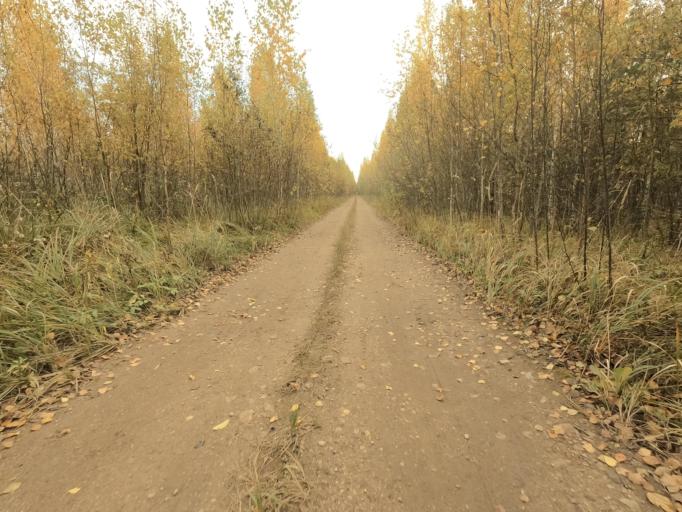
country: RU
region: Novgorod
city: Pankovka
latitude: 58.8762
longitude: 30.8708
